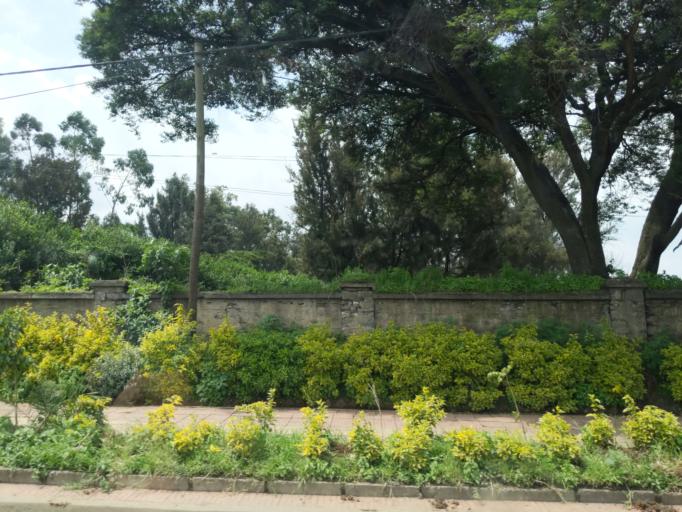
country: ET
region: Adis Abeba
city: Addis Ababa
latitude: 8.9702
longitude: 38.7618
